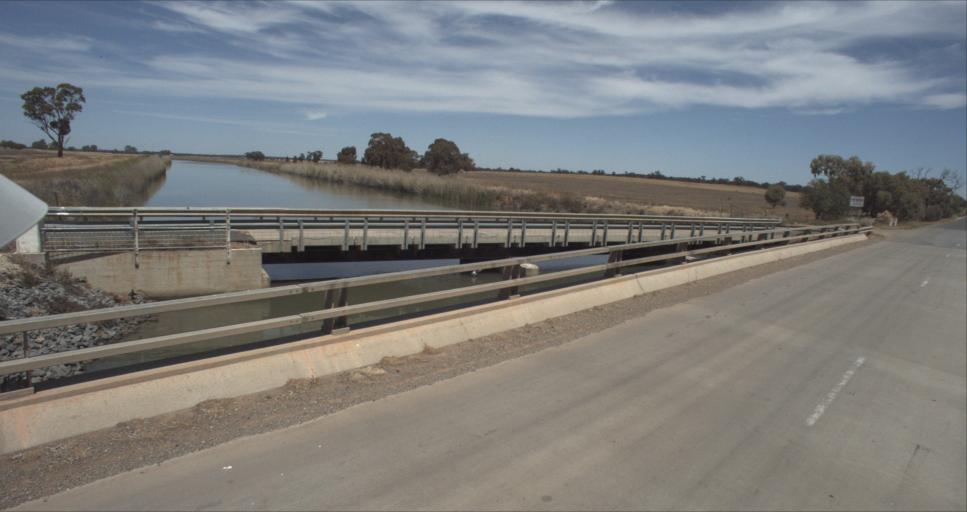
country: AU
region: New South Wales
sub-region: Leeton
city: Leeton
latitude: -34.6488
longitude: 146.4695
